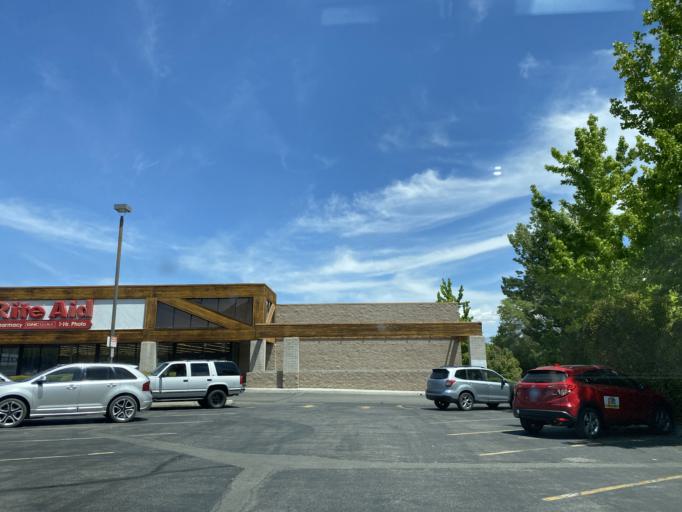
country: US
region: California
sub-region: Inyo County
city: Dixon Lane-Meadow Creek
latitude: 37.3767
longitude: -118.4206
